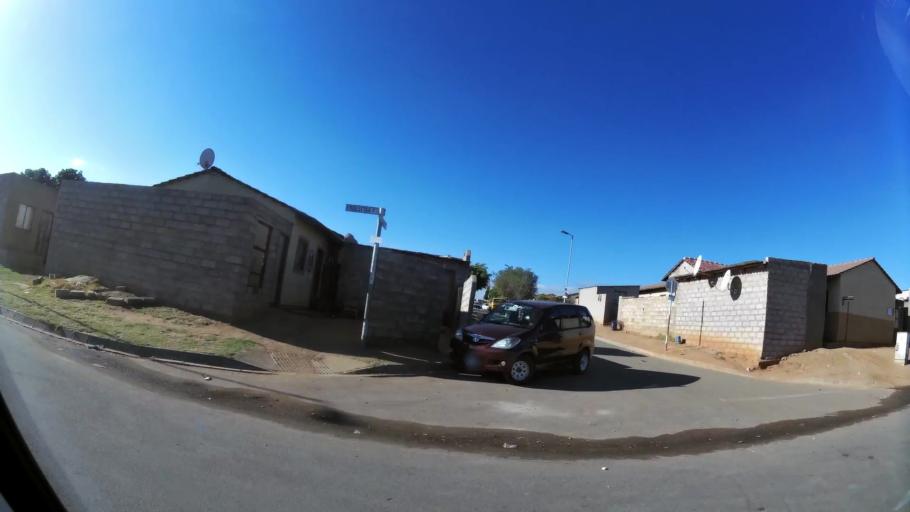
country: ZA
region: Gauteng
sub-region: City of Johannesburg Metropolitan Municipality
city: Diepsloot
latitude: -25.8993
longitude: 28.0968
